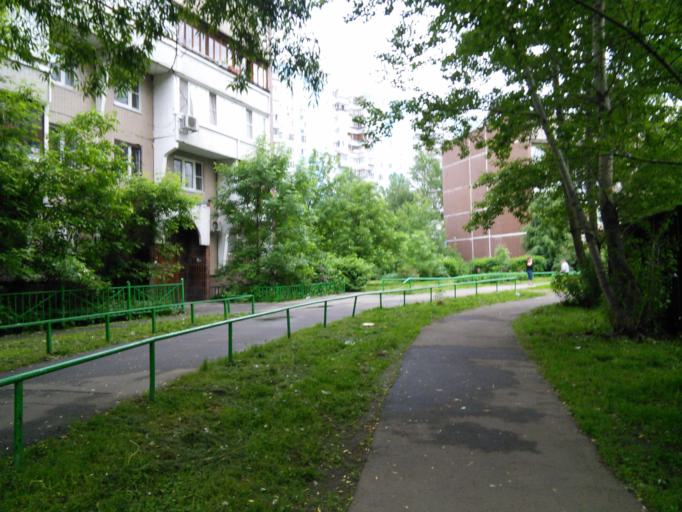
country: RU
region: Moscow
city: Brateyevo
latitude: 55.6514
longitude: 37.7537
